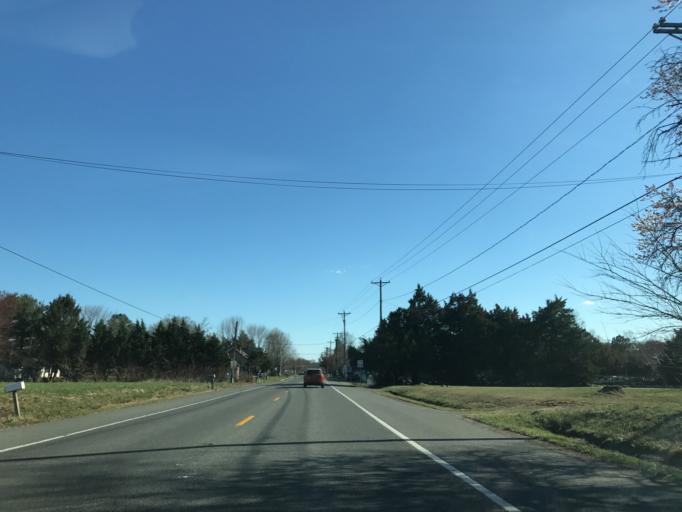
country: US
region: Maryland
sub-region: Caroline County
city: Greensboro
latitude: 39.1477
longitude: -75.8654
